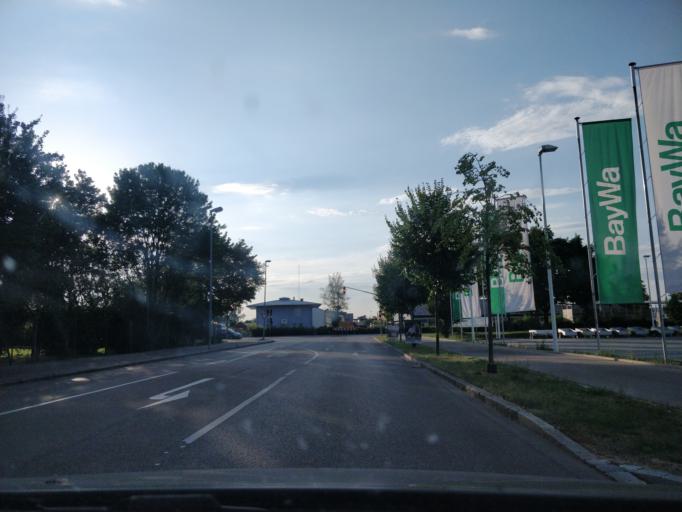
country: DE
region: Bavaria
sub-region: Swabia
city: Noerdlingen
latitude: 48.8603
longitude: 10.5036
